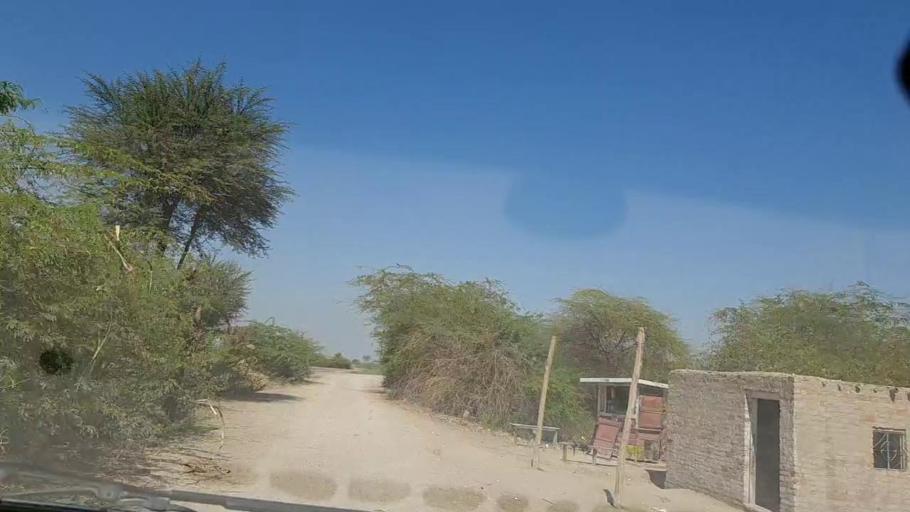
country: PK
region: Sindh
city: Mirpur Khas
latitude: 25.4248
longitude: 69.0420
